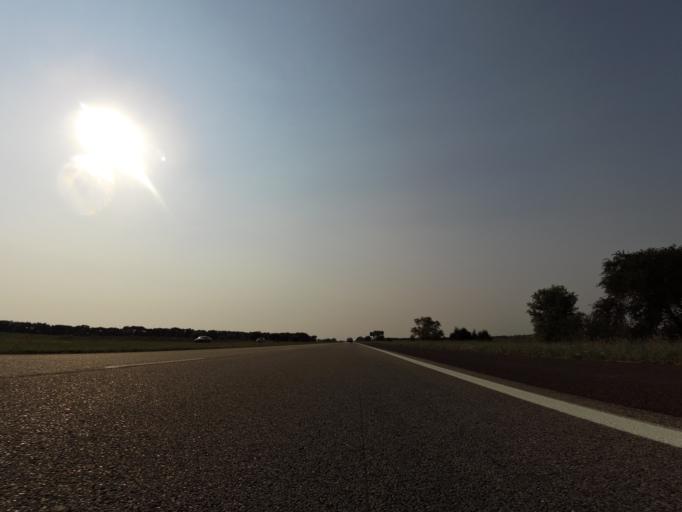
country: US
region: Kansas
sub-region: Reno County
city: Haven
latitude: 37.9136
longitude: -97.8160
